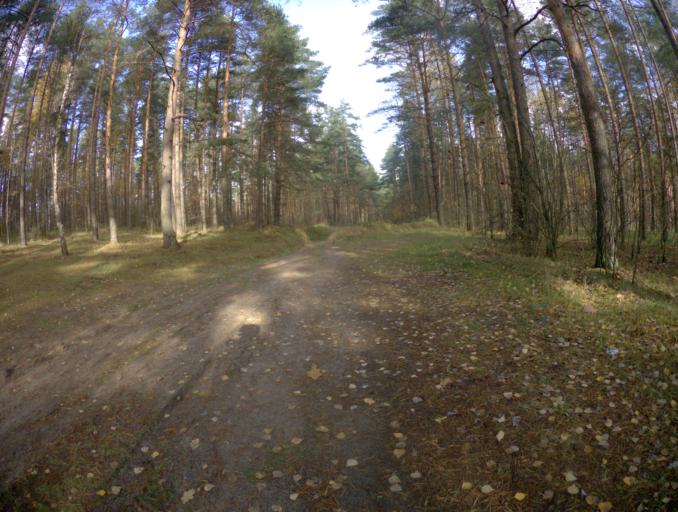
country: RU
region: Vladimir
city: Kommunar
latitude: 56.0692
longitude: 40.4417
